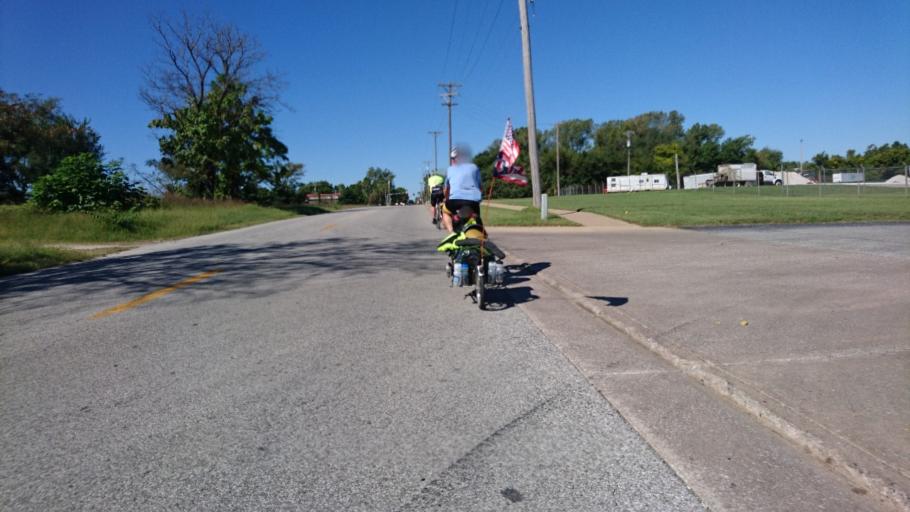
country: US
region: Missouri
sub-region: Jasper County
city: Joplin
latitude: 37.0901
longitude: -94.5277
